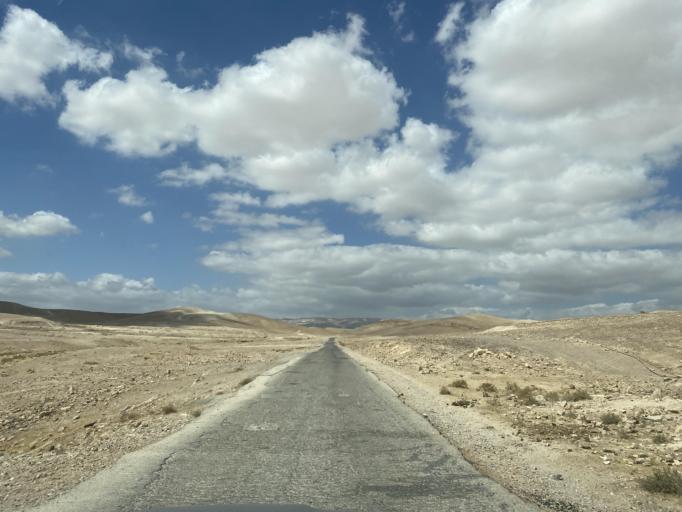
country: PS
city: `Arab ar Rashaydah
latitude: 31.5330
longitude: 35.2824
